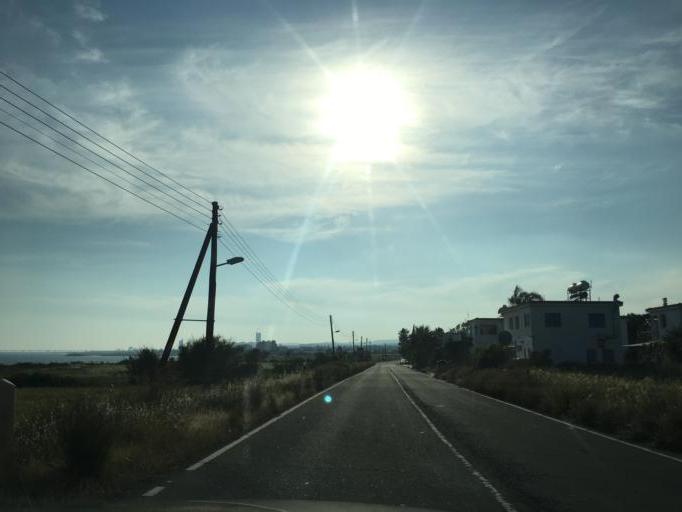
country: CY
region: Larnaka
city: Kofinou
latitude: 34.7327
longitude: 33.3554
